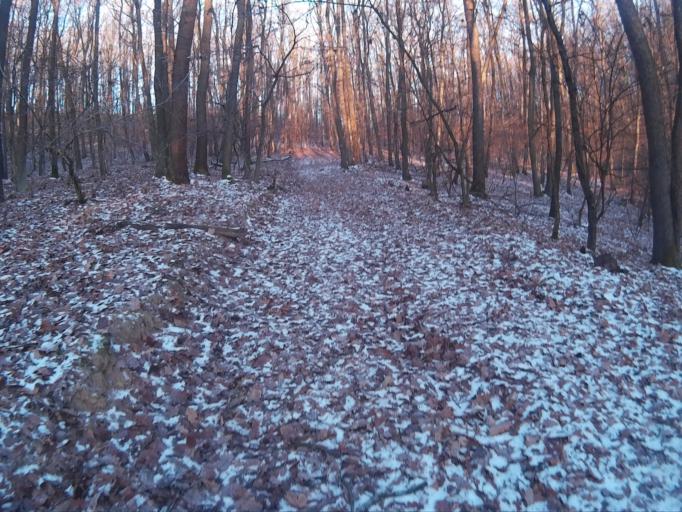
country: HU
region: Borsod-Abauj-Zemplen
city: Putnok
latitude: 48.3335
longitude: 20.4278
